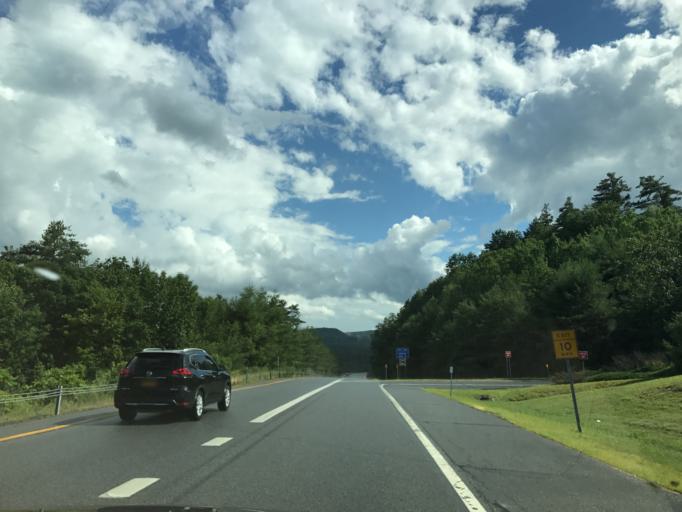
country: US
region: New York
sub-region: Warren County
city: Warrensburg
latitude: 43.4281
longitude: -73.7217
